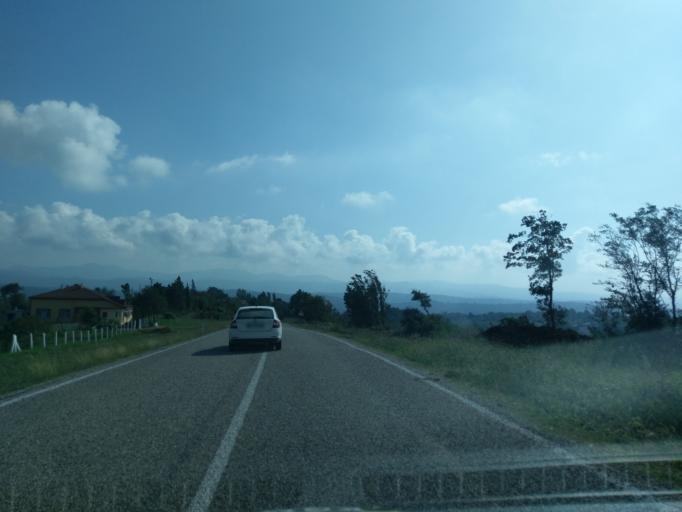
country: TR
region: Sinop
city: Erfelek
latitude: 41.9716
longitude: 34.8632
